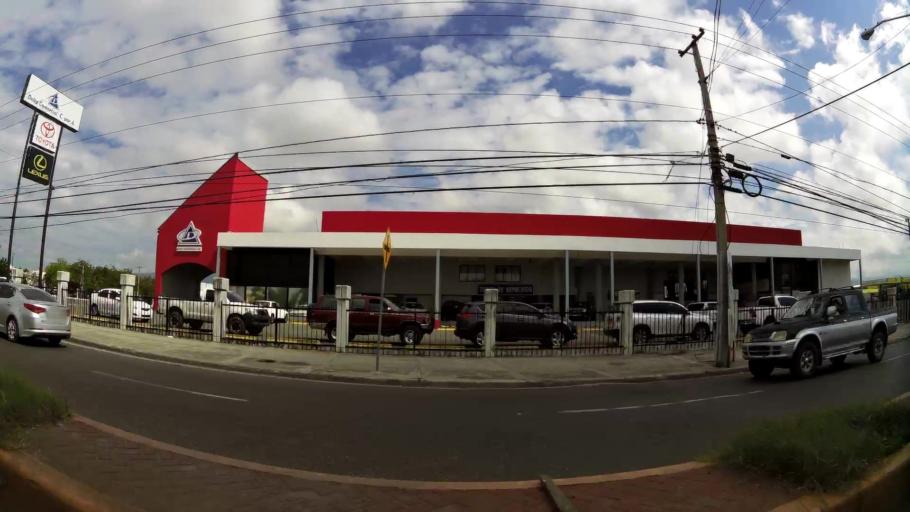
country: DO
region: Santiago
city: Santiago de los Caballeros
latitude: 19.4892
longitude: -70.7178
